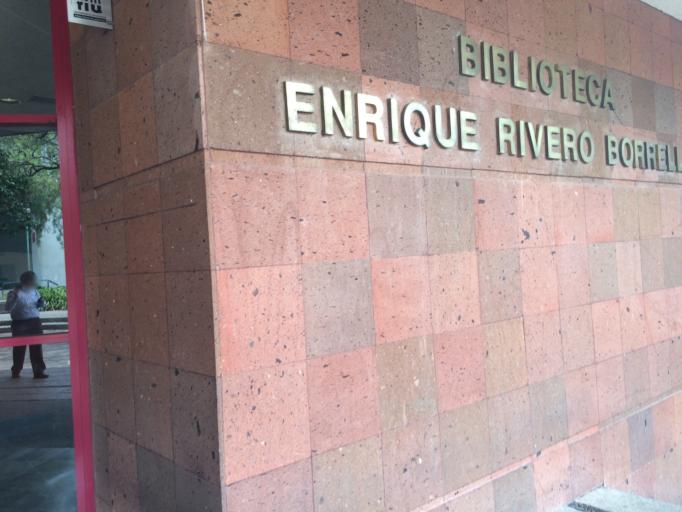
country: MX
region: Mexico City
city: Magdalena Contreras
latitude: 19.3257
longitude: -99.1826
